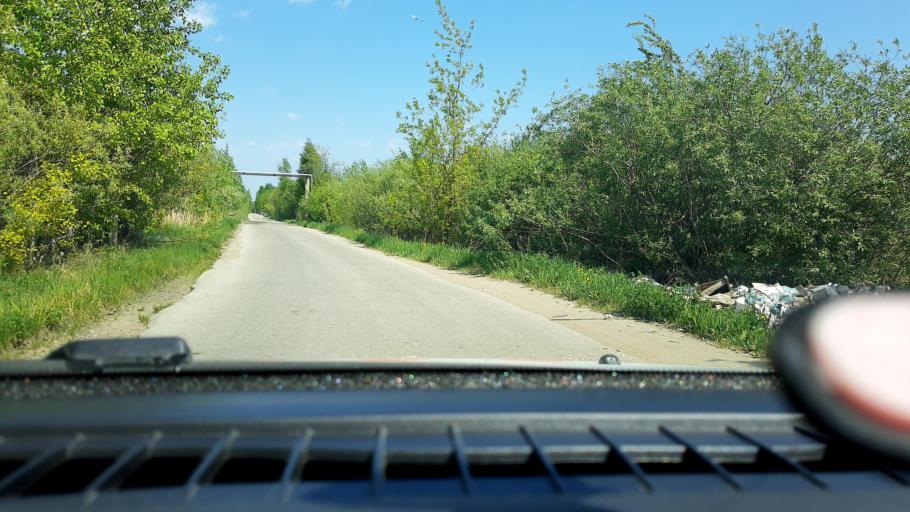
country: RU
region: Nizjnij Novgorod
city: Kstovo
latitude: 56.1360
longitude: 44.1293
